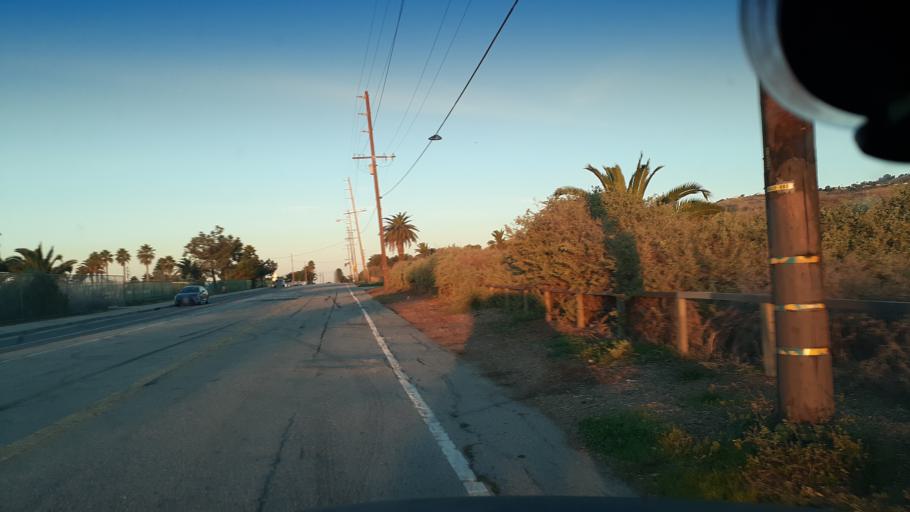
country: US
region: California
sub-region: Los Angeles County
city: San Pedro
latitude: 33.7157
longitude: -118.3150
